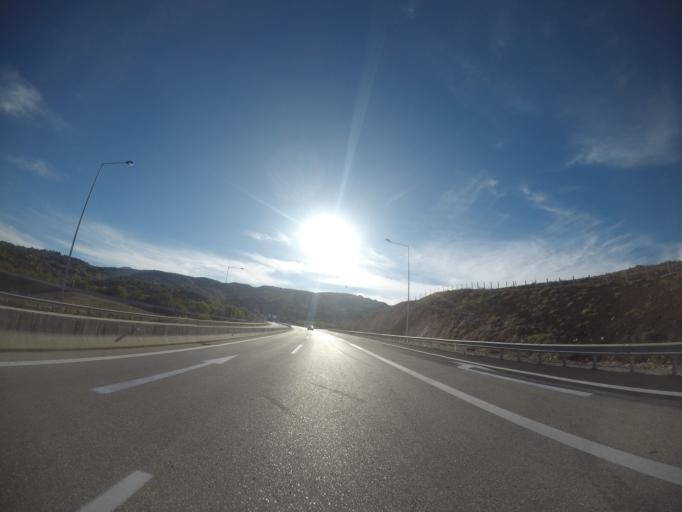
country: GR
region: Epirus
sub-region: Nomos Ioanninon
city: Pedini
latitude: 39.5901
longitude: 20.8205
